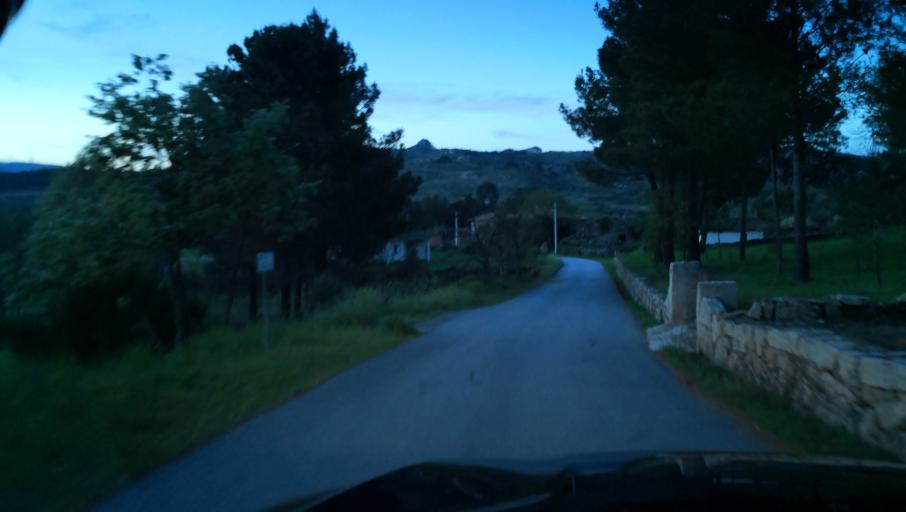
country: PT
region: Vila Real
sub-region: Vila Real
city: Vila Real
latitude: 41.3532
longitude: -7.6899
